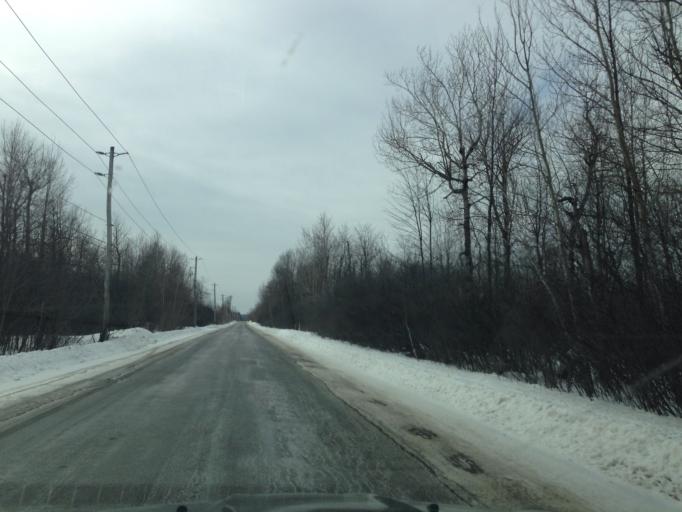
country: CA
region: Ontario
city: Ottawa
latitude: 45.3292
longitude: -75.5548
